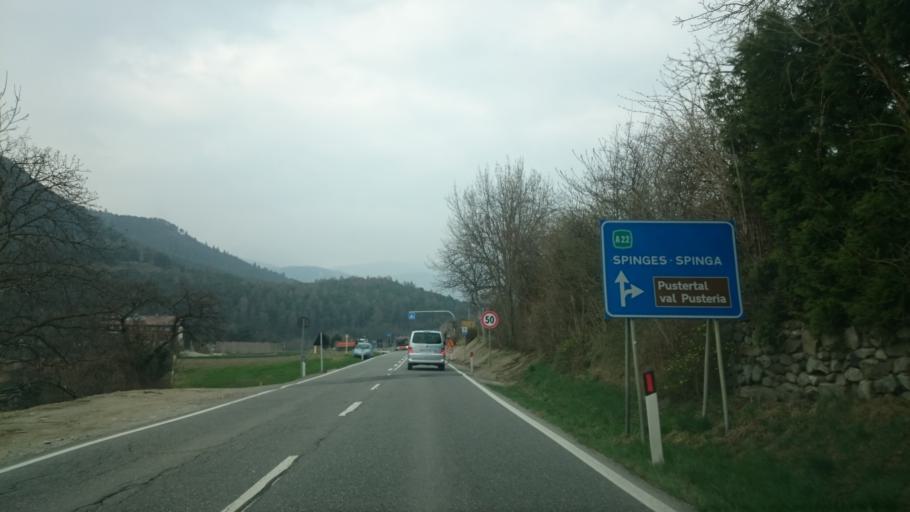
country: IT
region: Trentino-Alto Adige
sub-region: Bolzano
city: Naz-Sciaves - Natz-Schabs
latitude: 46.7709
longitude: 11.6648
